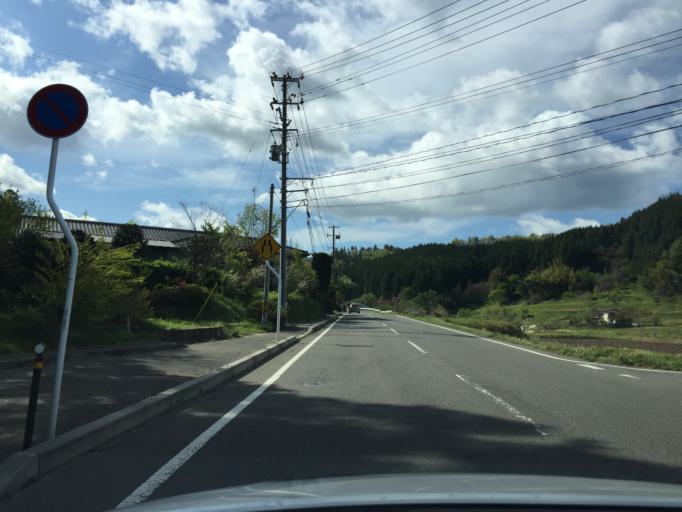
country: JP
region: Fukushima
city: Fukushima-shi
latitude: 37.6495
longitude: 140.6129
